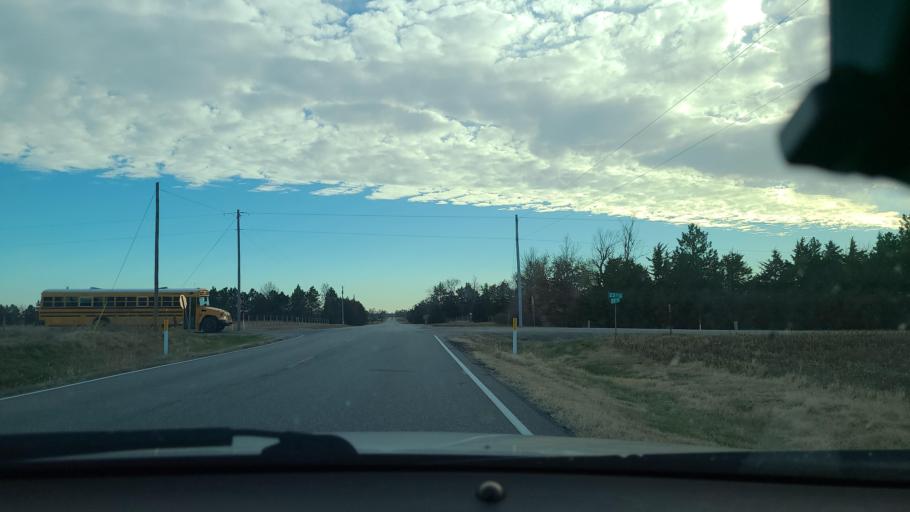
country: US
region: Kansas
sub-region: Sedgwick County
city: Goddard
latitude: 37.6501
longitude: -97.5894
